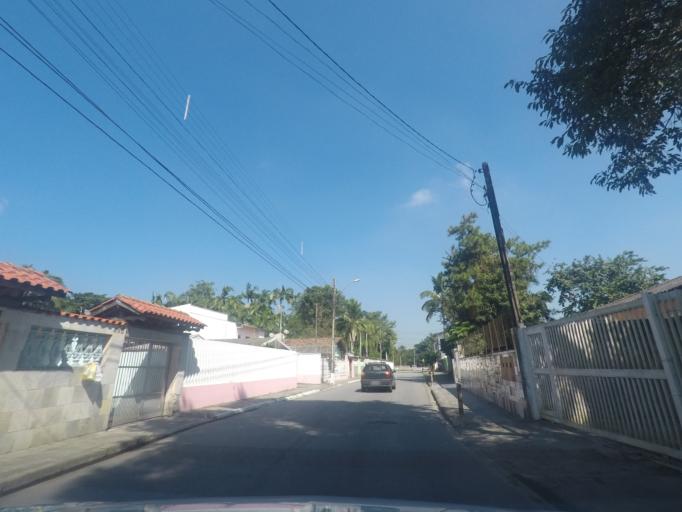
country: BR
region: Parana
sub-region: Paranagua
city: Paranagua
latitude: -25.5286
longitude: -48.5151
